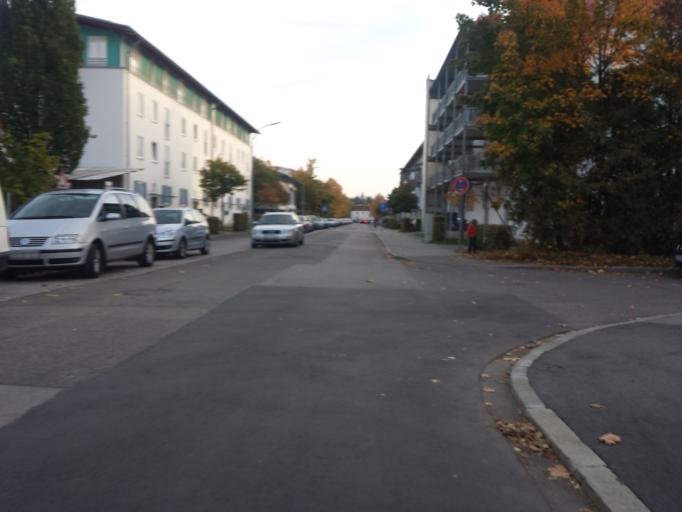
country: DE
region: Bavaria
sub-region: Upper Bavaria
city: Ingolstadt
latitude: 48.7776
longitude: 11.4203
